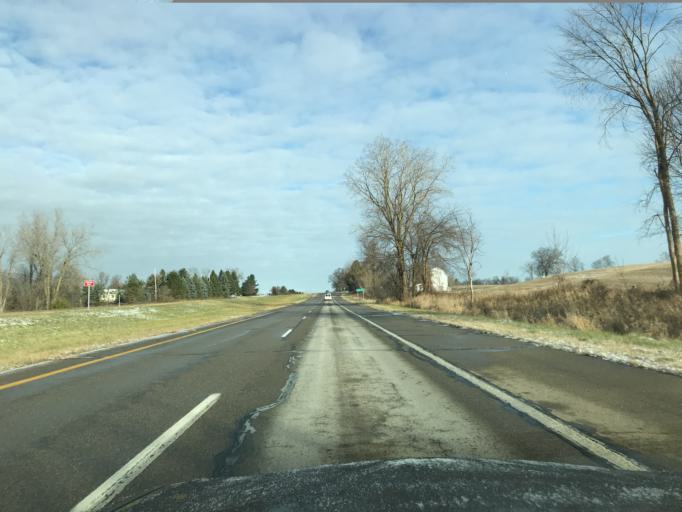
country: US
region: Michigan
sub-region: Eaton County
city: Dimondale
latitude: 42.6003
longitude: -84.6222
